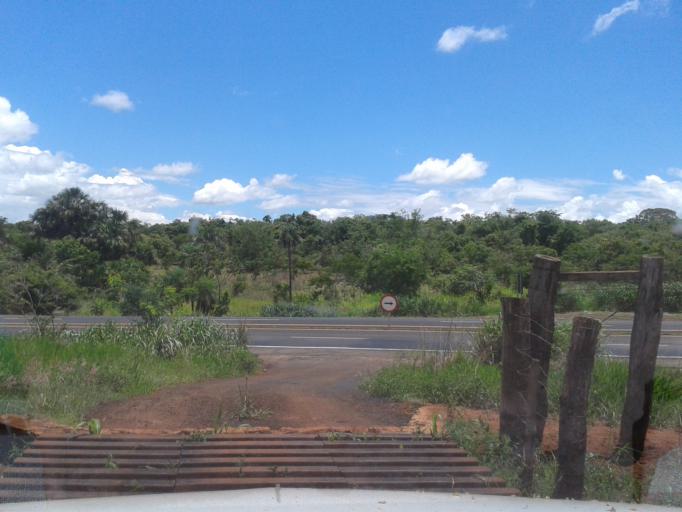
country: BR
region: Minas Gerais
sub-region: Centralina
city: Centralina
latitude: -18.6646
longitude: -49.1660
